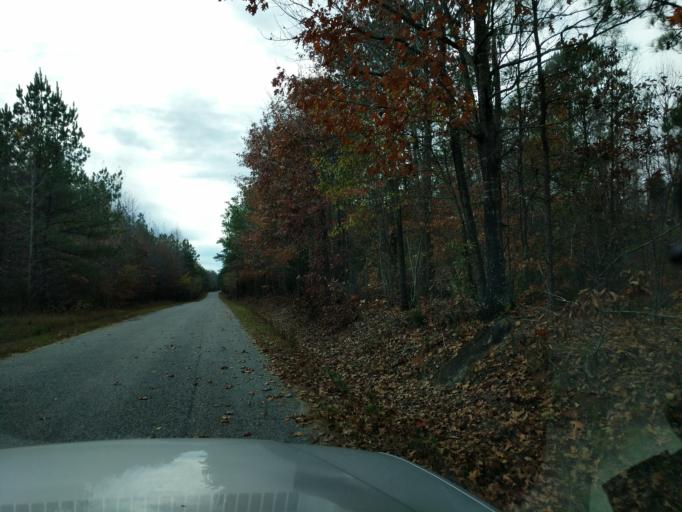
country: US
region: South Carolina
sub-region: Laurens County
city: Watts Mills
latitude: 34.5427
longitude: -81.9406
